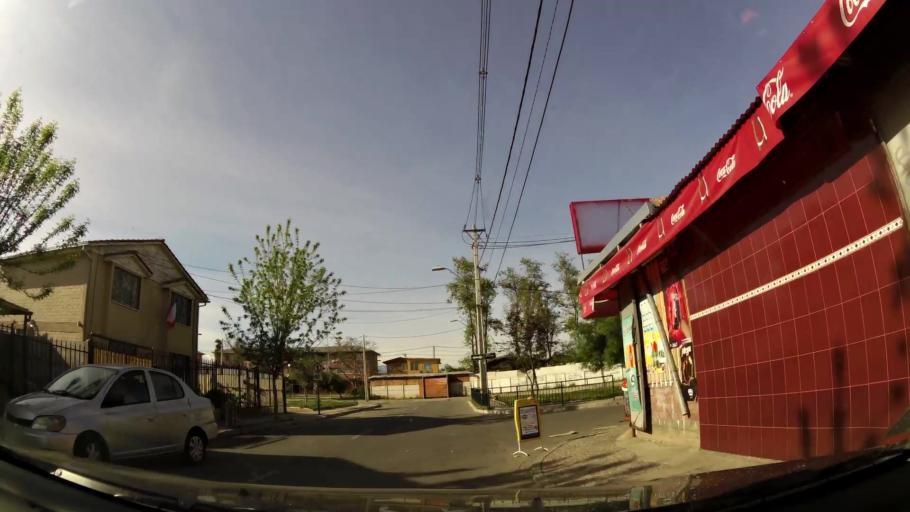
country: CL
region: Santiago Metropolitan
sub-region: Provincia de Cordillera
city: Puente Alto
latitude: -33.6137
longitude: -70.5947
